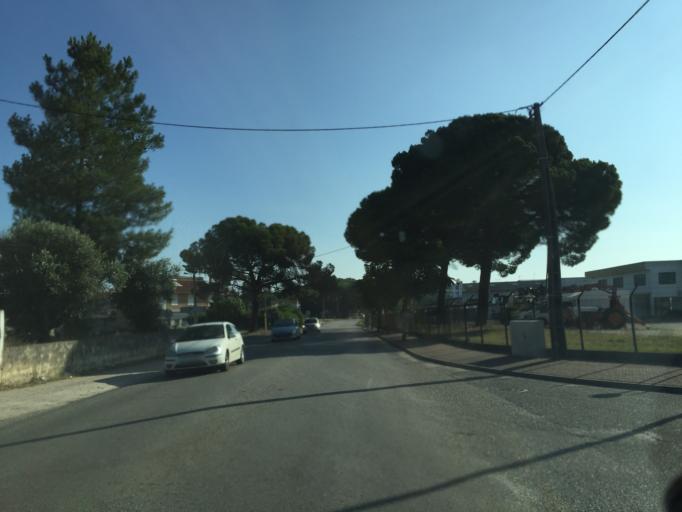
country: PT
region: Santarem
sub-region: Abrantes
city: Alferrarede
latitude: 39.4826
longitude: -8.1865
